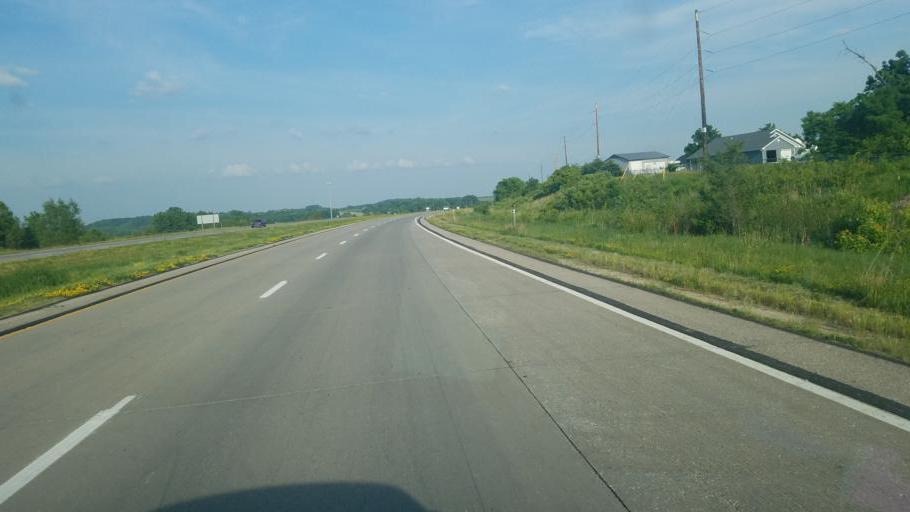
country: US
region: Iowa
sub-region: Marshall County
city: Marshalltown
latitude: 42.0111
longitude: -92.7765
